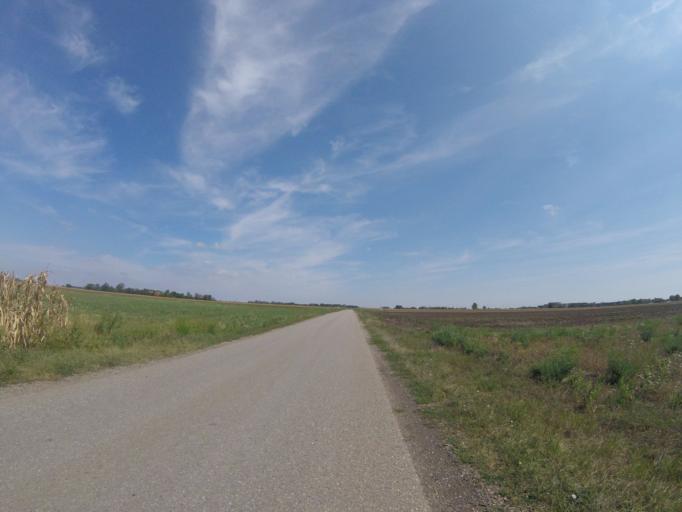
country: AT
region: Burgenland
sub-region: Politischer Bezirk Neusiedl am See
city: Frauenkirchen
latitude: 47.8066
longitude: 16.9022
